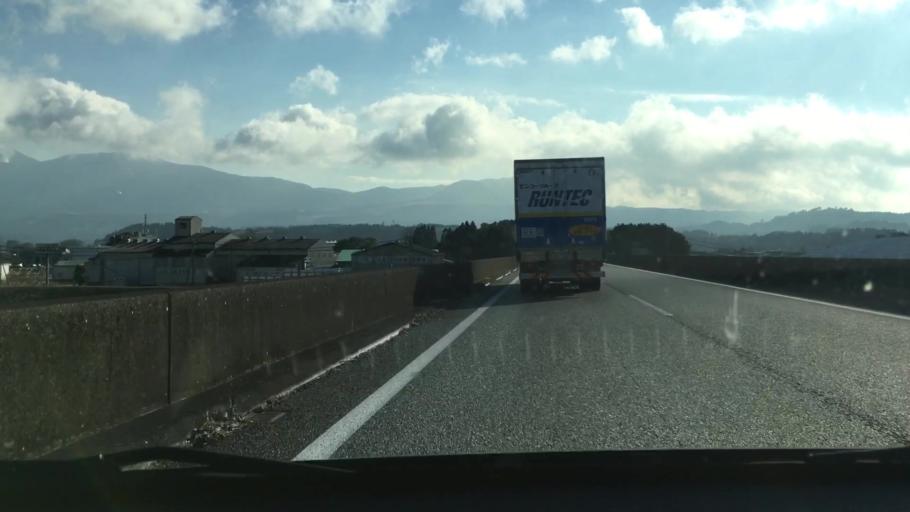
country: JP
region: Kumamoto
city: Hitoyoshi
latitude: 32.0545
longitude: 130.8022
